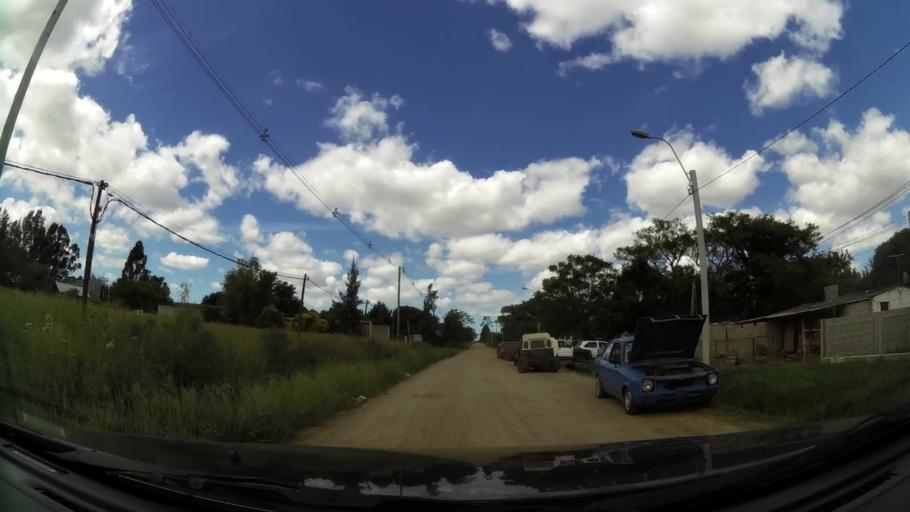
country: UY
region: Canelones
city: Colonia Nicolich
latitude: -34.8109
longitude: -56.0442
